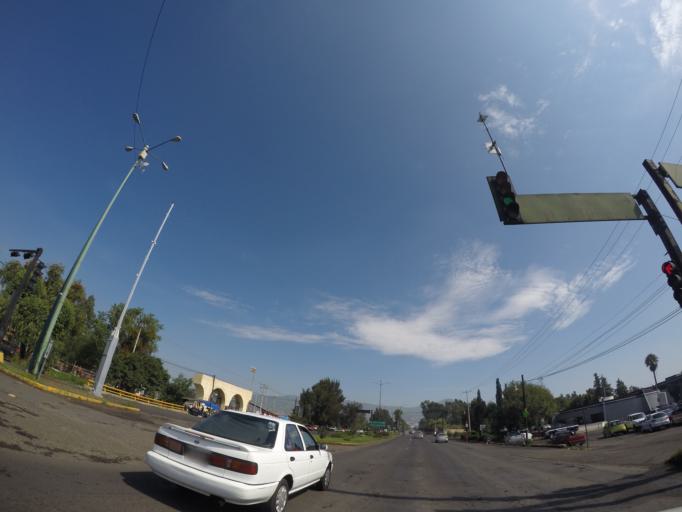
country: MX
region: Michoacan
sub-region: Morelia
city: Morelos
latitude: 19.6811
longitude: -101.2353
